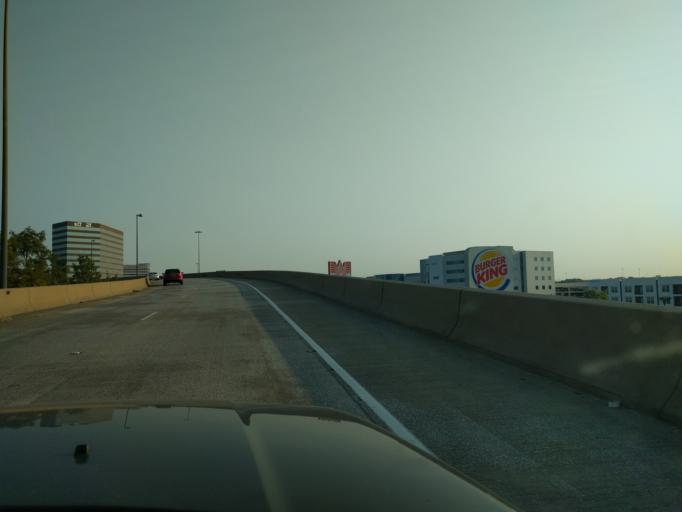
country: US
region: Texas
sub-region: Dallas County
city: Richardson
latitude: 32.9099
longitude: -96.7684
